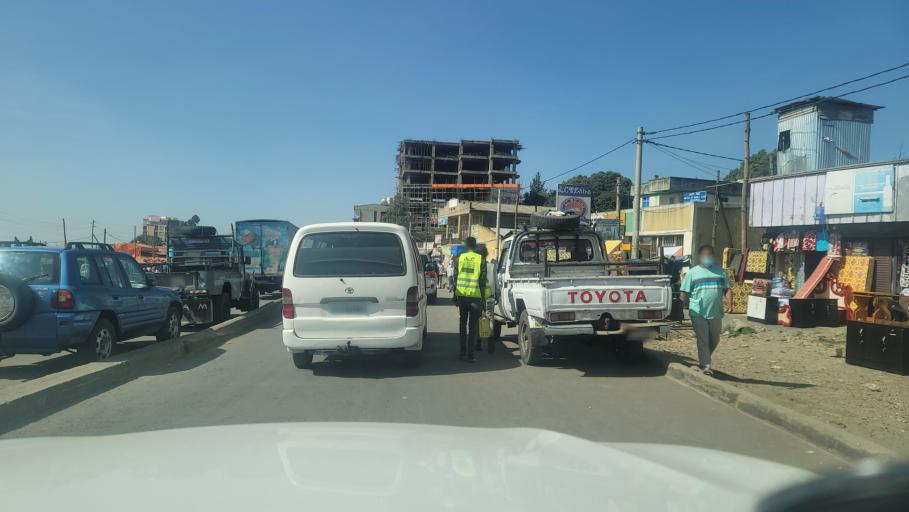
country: ET
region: Adis Abeba
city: Addis Ababa
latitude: 9.0373
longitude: 38.8304
